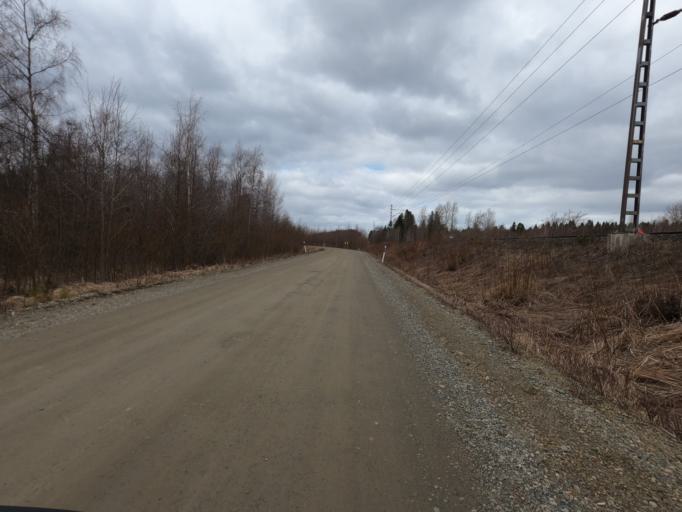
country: FI
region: North Karelia
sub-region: Joensuu
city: Joensuu
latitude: 62.5654
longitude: 29.8025
